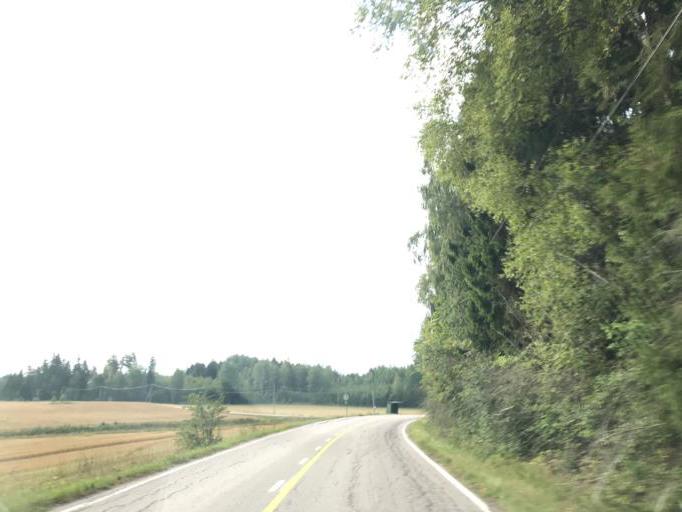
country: FI
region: Uusimaa
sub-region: Helsinki
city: Vihti
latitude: 60.3835
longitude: 24.5242
